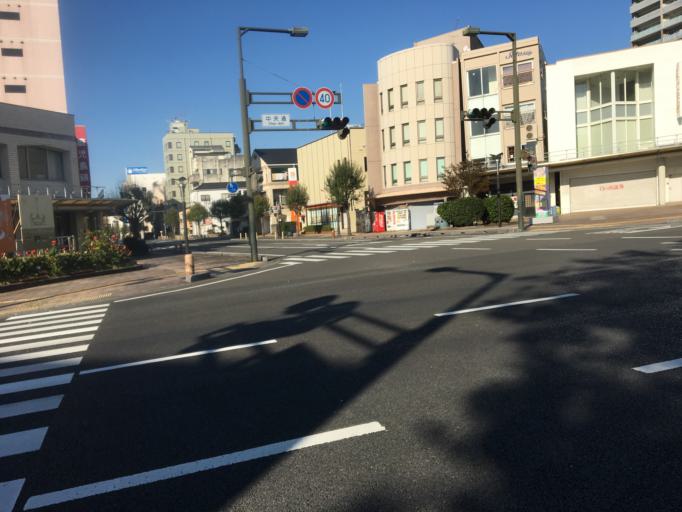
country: JP
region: Miyazaki
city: Nobeoka
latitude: 32.5821
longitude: 131.6687
